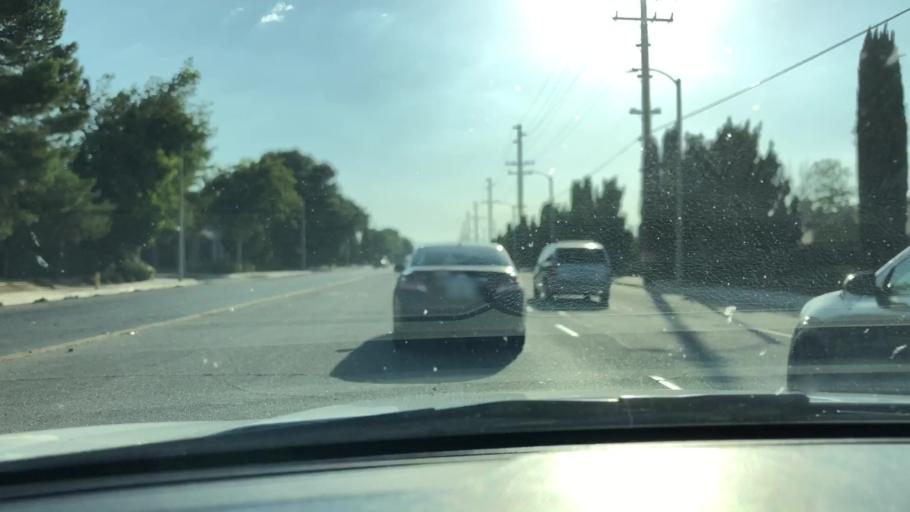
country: US
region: California
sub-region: Los Angeles County
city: Quartz Hill
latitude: 34.6748
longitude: -118.1968
